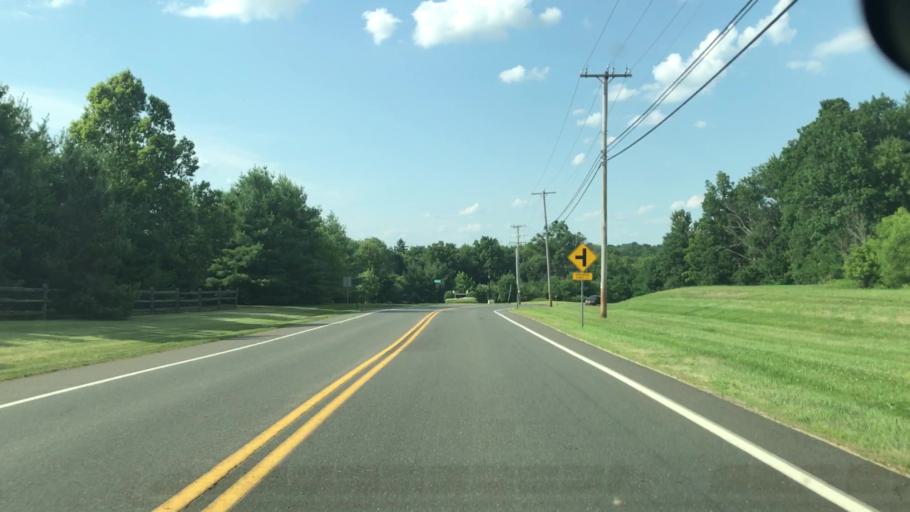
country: US
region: New Jersey
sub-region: Hunterdon County
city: Flemington
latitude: 40.4644
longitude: -74.8293
